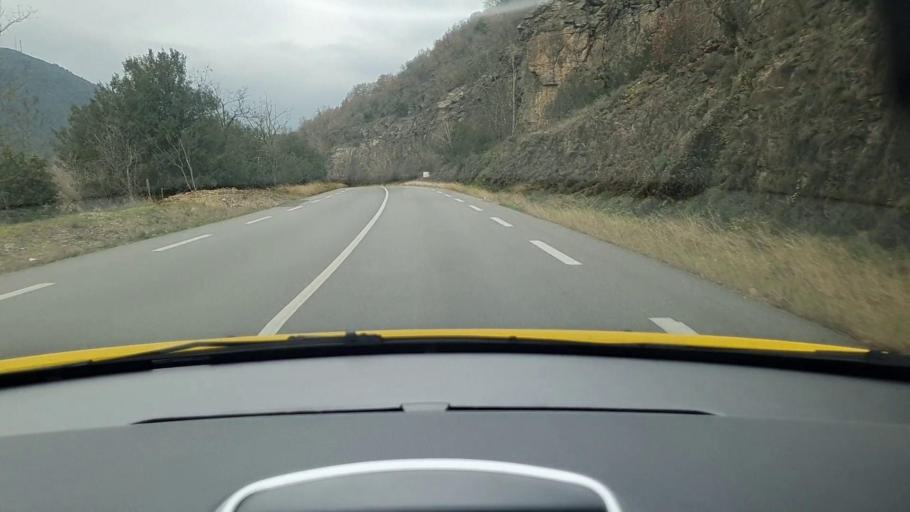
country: FR
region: Languedoc-Roussillon
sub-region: Departement du Gard
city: Besseges
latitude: 44.2810
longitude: 4.1285
